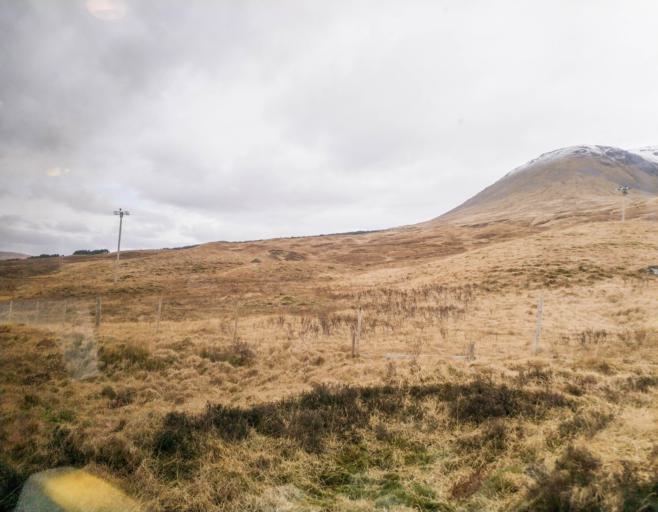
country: GB
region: Scotland
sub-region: Highland
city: Spean Bridge
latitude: 56.5123
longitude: -4.7612
